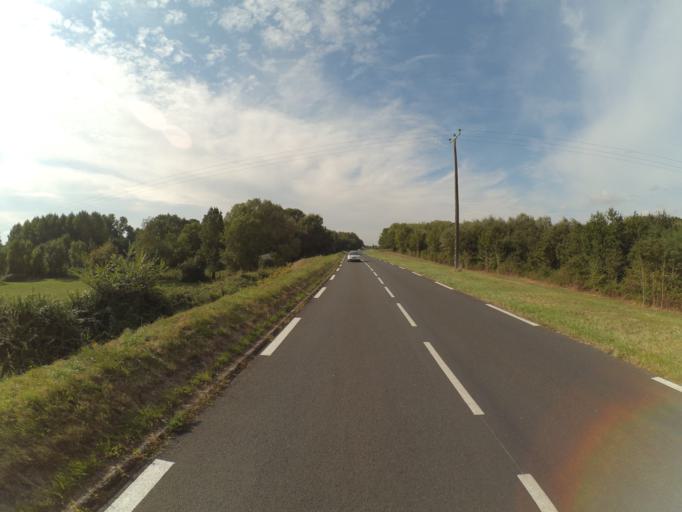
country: FR
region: Centre
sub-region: Departement d'Indre-et-Loire
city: Chouze-sur-Loire
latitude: 47.2329
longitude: 0.1099
